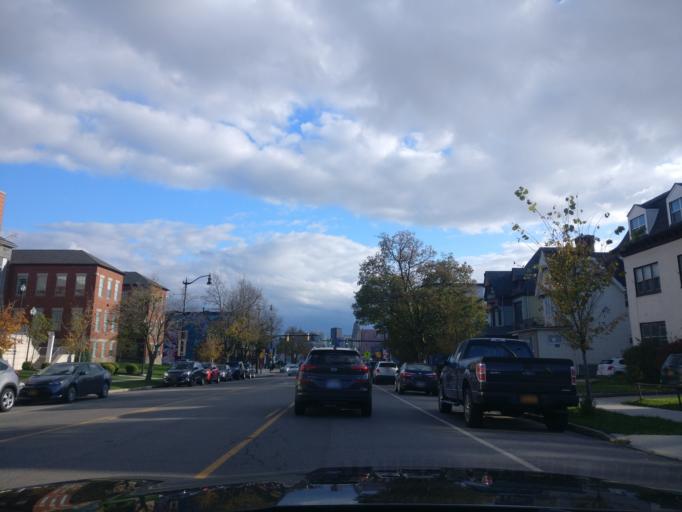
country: US
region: New York
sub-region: Erie County
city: Buffalo
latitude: 42.9004
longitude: -78.8914
